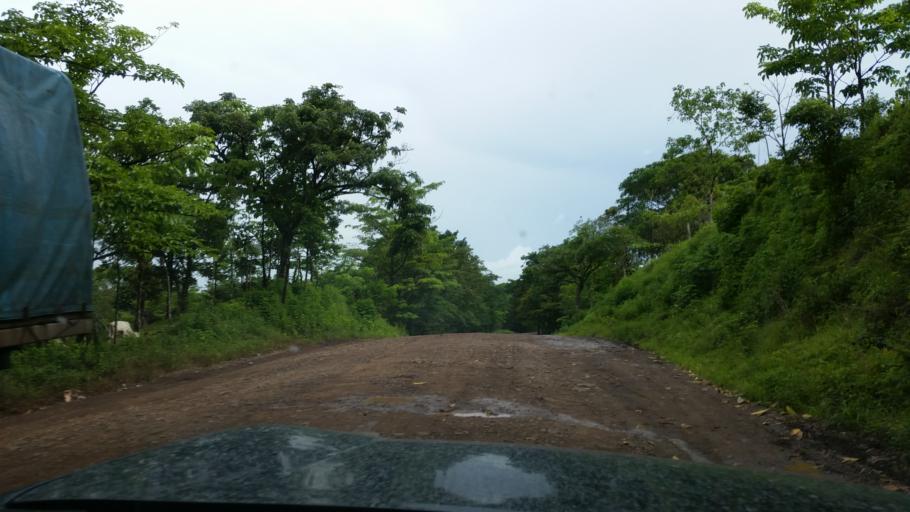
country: NI
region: Atlantico Norte (RAAN)
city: Siuna
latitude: 13.4521
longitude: -84.8538
